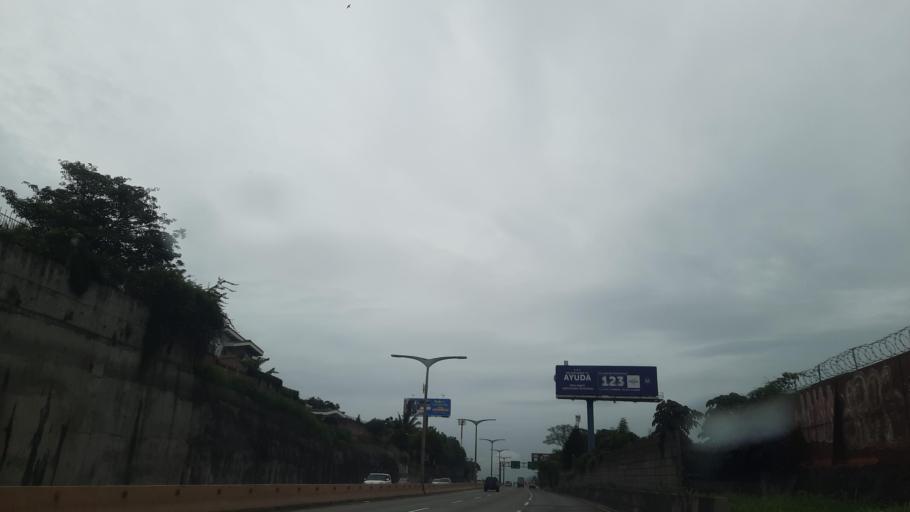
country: SV
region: La Libertad
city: Santa Tecla
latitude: 13.6845
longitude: -89.2759
